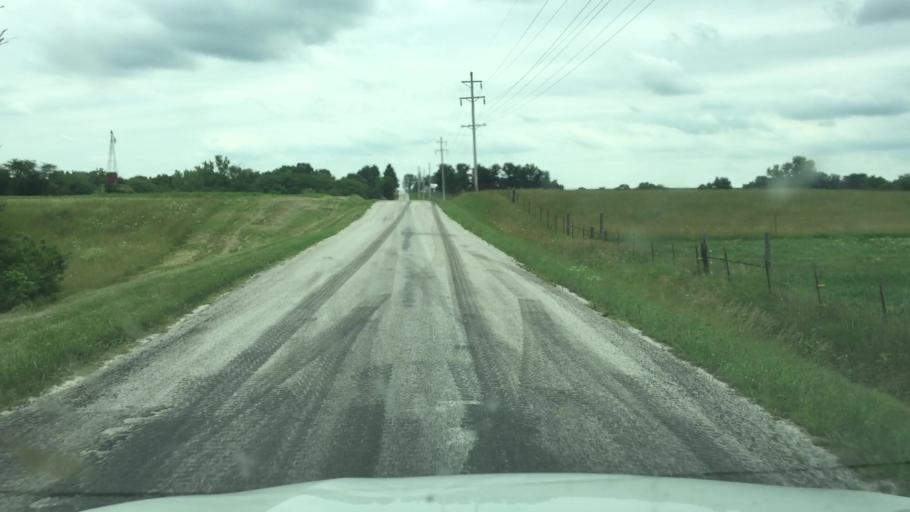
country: US
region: Illinois
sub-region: Hancock County
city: Carthage
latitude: 40.3296
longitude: -91.0825
